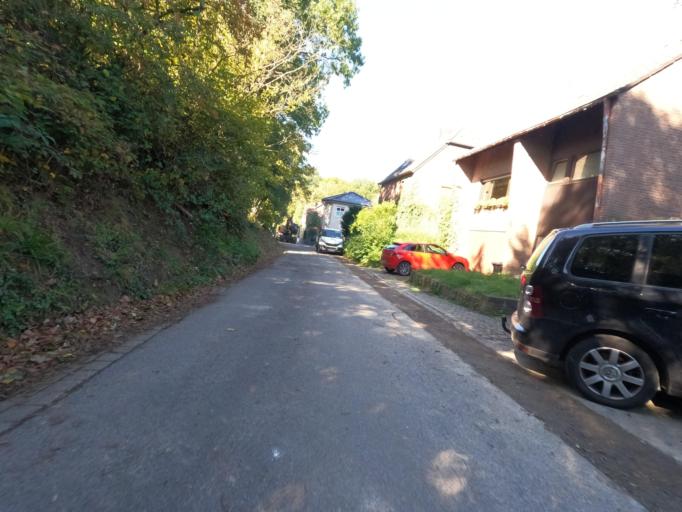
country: DE
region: North Rhine-Westphalia
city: Huckelhoven
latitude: 51.0490
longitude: 6.2563
